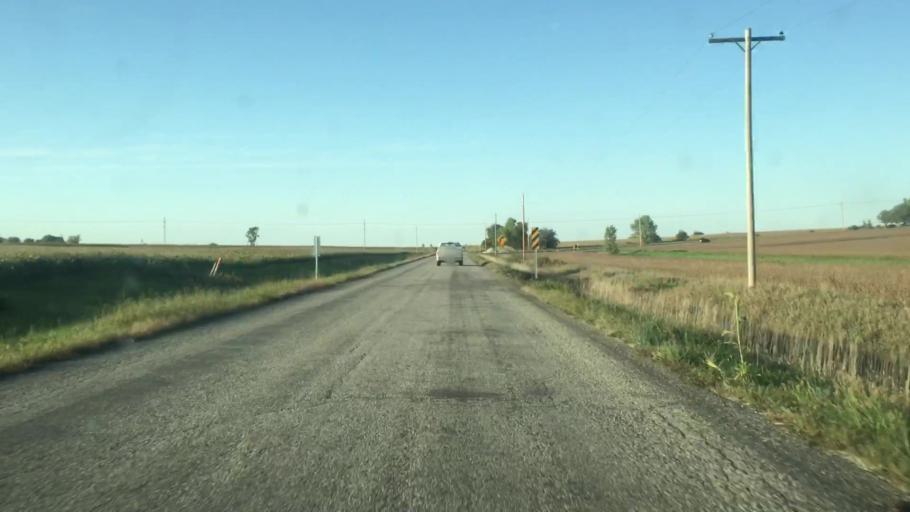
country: US
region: Kansas
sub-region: Brown County
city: Horton
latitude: 39.5625
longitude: -95.4020
